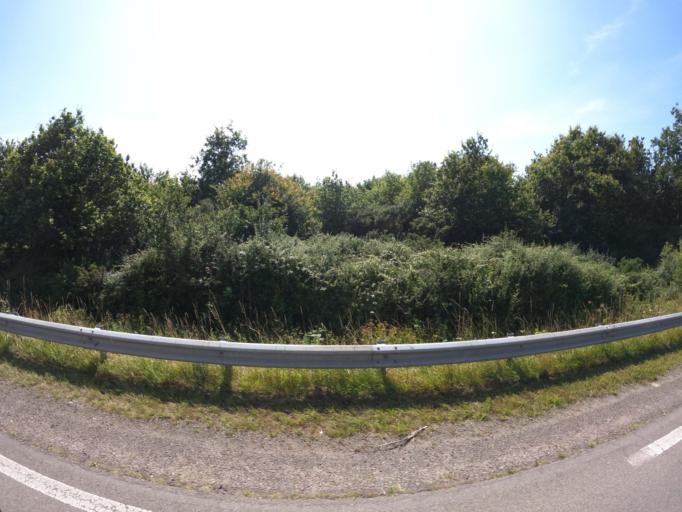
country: FR
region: Pays de la Loire
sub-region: Departement de la Loire-Atlantique
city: La Bernerie-en-Retz
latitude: 47.0945
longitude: -2.0355
